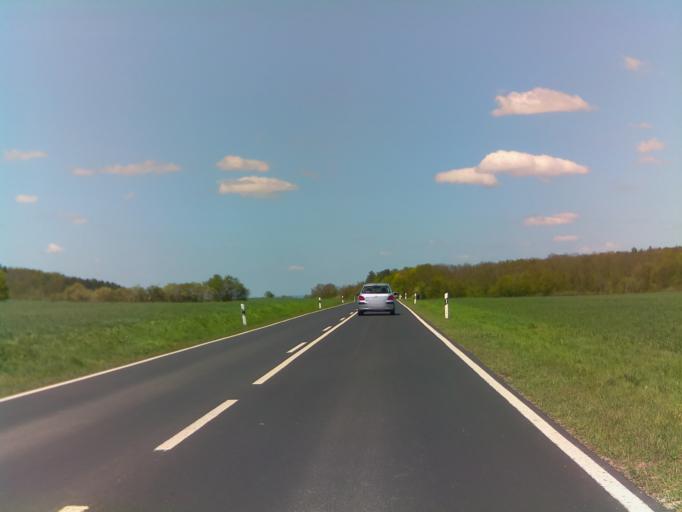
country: DE
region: Thuringia
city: Dornheim
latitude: 50.8062
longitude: 10.9788
